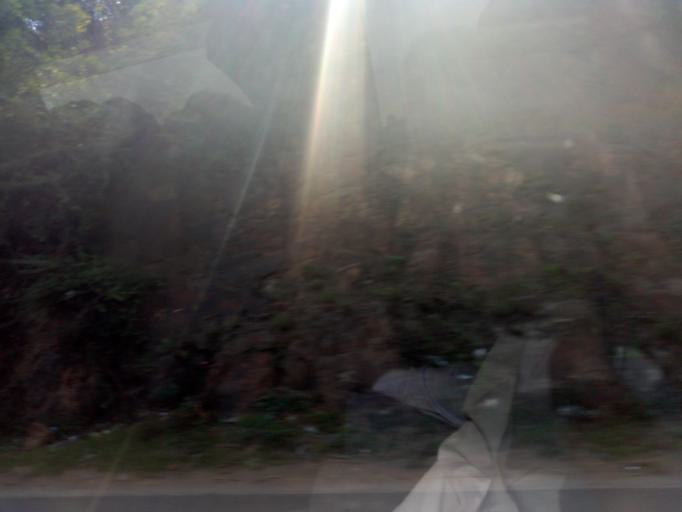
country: KE
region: Nakuru
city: Kijabe
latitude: -1.0140
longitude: 36.6009
